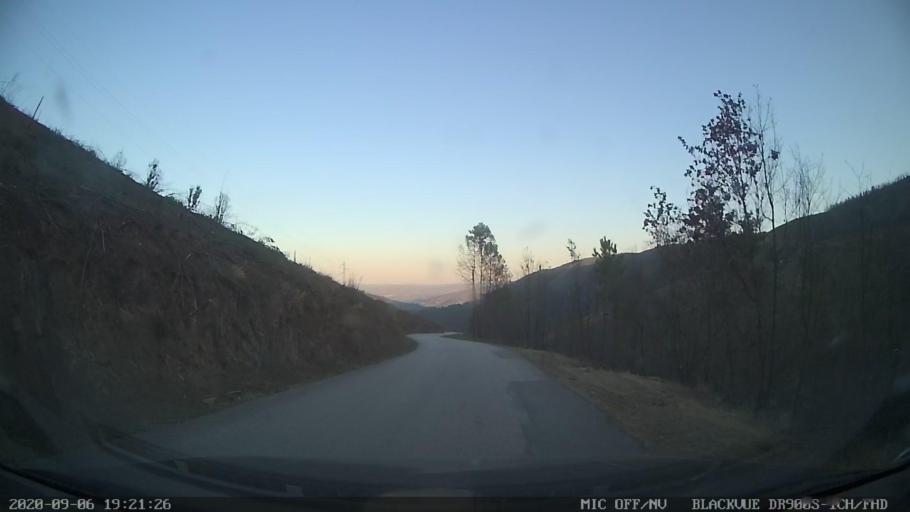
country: PT
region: Vila Real
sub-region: Mesao Frio
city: Mesao Frio
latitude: 41.1834
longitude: -7.9311
